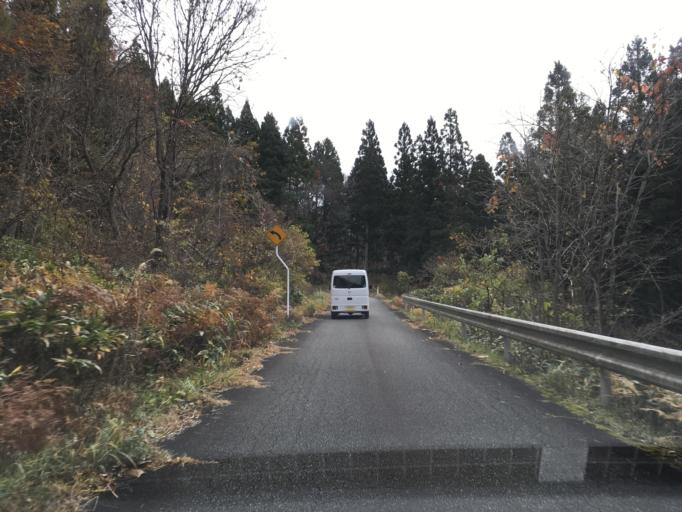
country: JP
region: Iwate
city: Mizusawa
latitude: 39.1248
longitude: 141.3211
